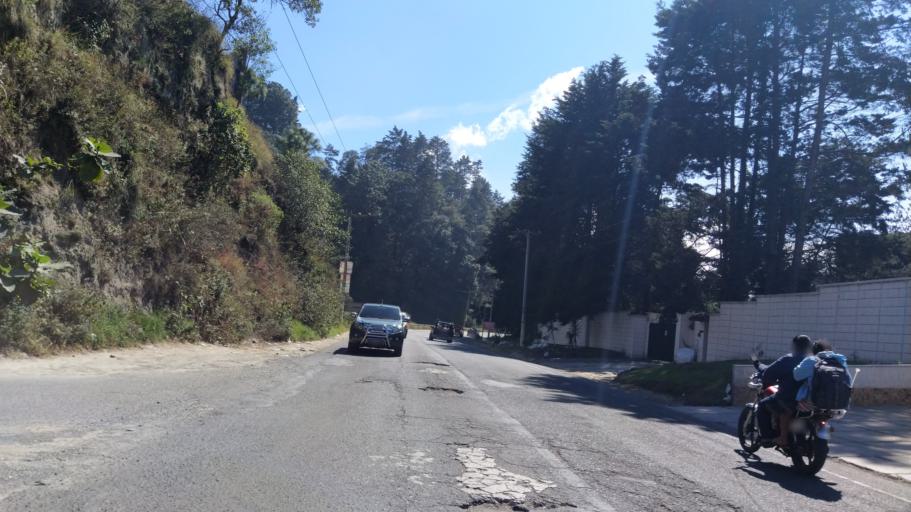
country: GT
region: Quetzaltenango
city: Cantel
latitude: 14.8203
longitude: -91.4527
